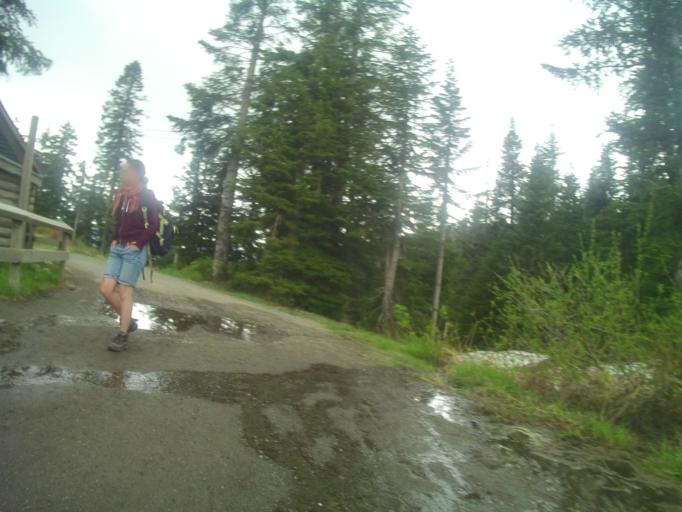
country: CA
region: British Columbia
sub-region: Fraser Valley Regional District
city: North Vancouver
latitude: 49.3831
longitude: -123.0786
